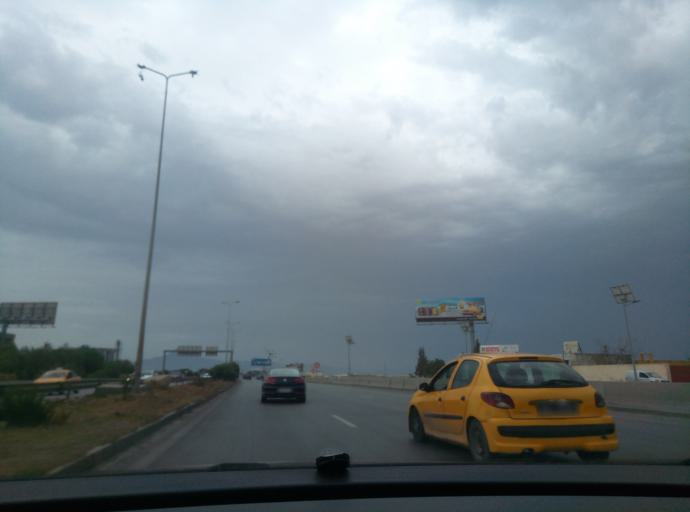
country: TN
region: Bin 'Arus
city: Ben Arous
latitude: 36.7335
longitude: 10.2257
